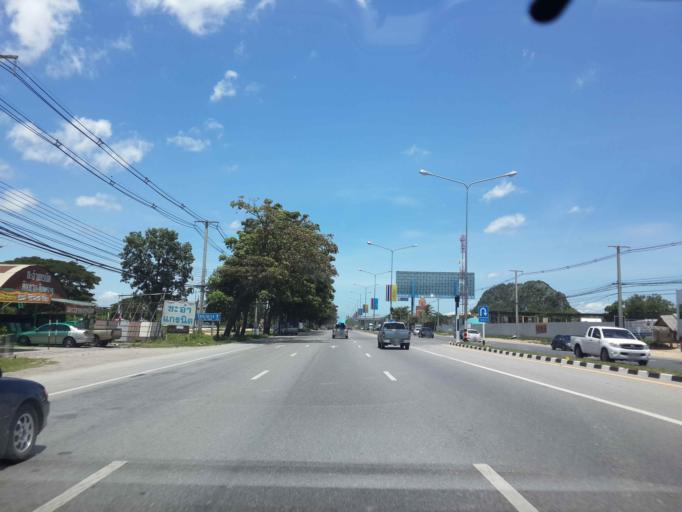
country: TH
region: Phetchaburi
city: Cha-am
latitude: 12.8191
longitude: 99.9398
